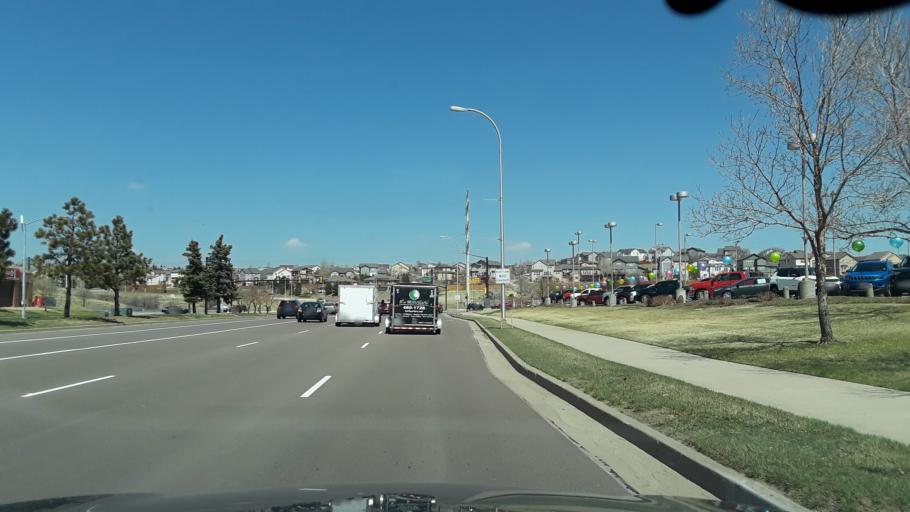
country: US
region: Colorado
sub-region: El Paso County
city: Black Forest
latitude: 38.9388
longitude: -104.7394
